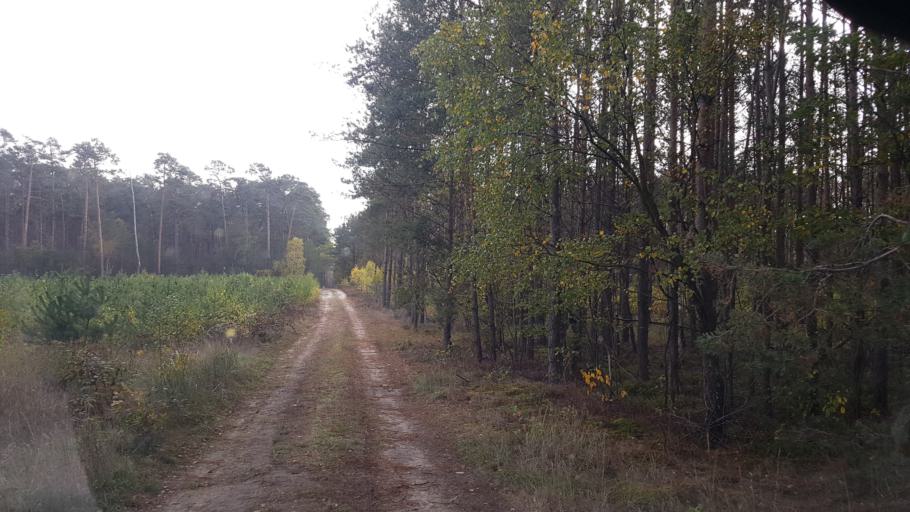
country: DE
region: Brandenburg
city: Schonborn
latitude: 51.6619
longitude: 13.4779
